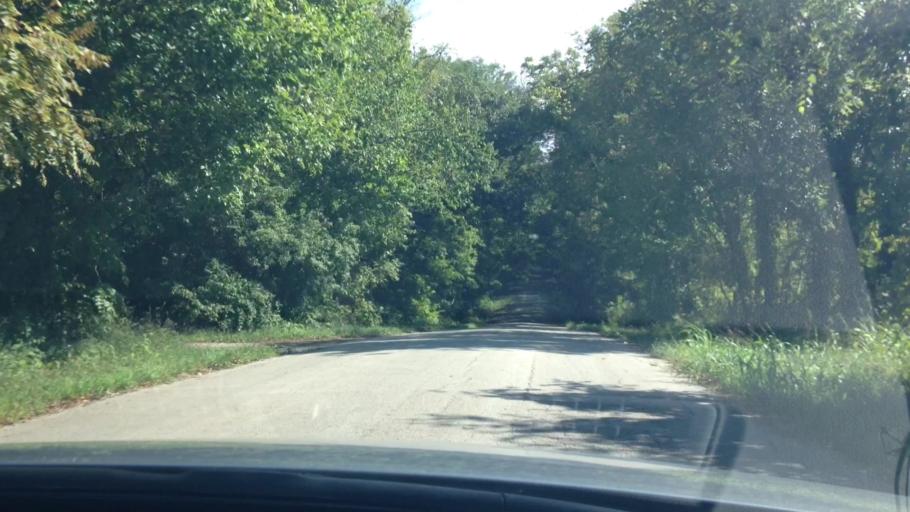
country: US
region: Missouri
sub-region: Platte County
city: Weatherby Lake
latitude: 39.3327
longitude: -94.6675
